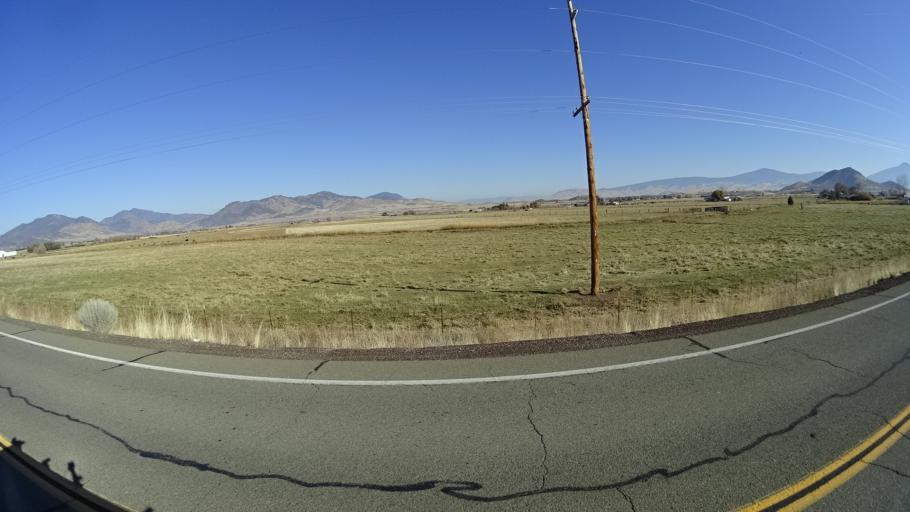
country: US
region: California
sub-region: Siskiyou County
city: Montague
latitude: 41.7061
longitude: -122.5657
